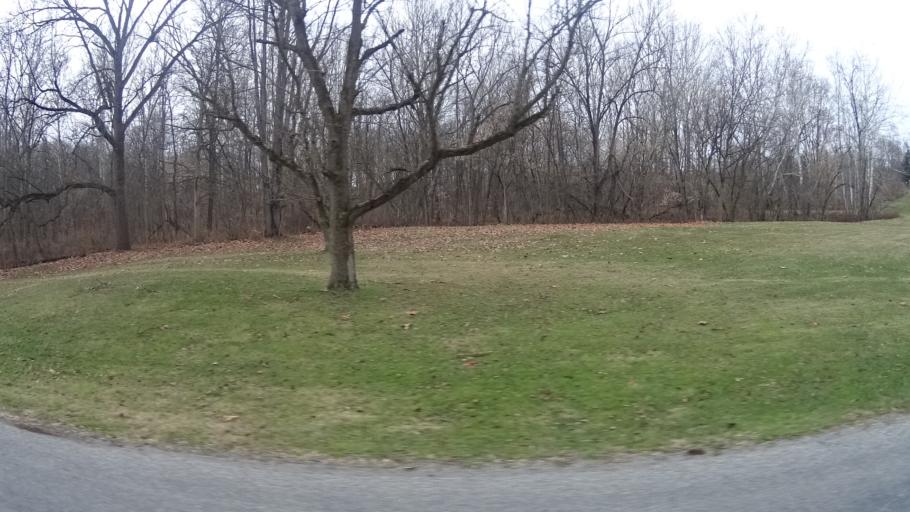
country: US
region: Ohio
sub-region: Lorain County
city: Wellington
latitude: 41.1863
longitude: -82.2423
